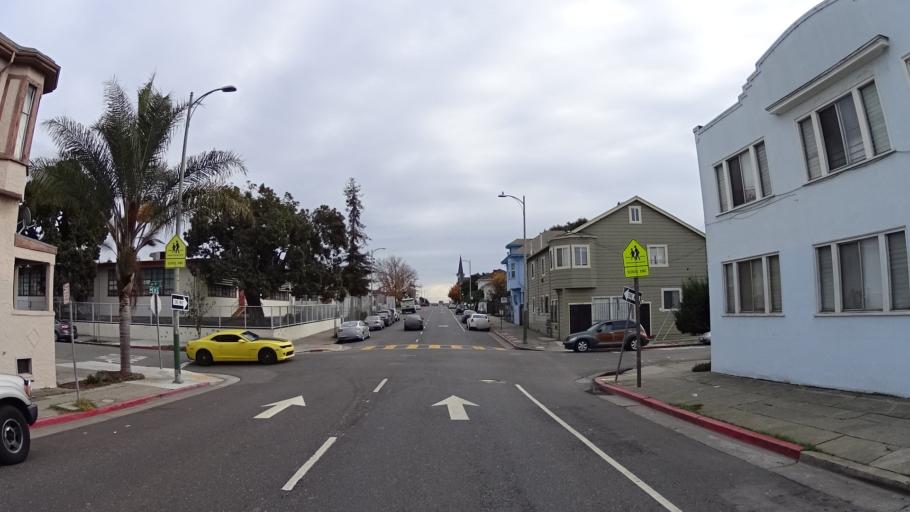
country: US
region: California
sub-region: Alameda County
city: Oakland
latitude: 37.7936
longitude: -122.2499
